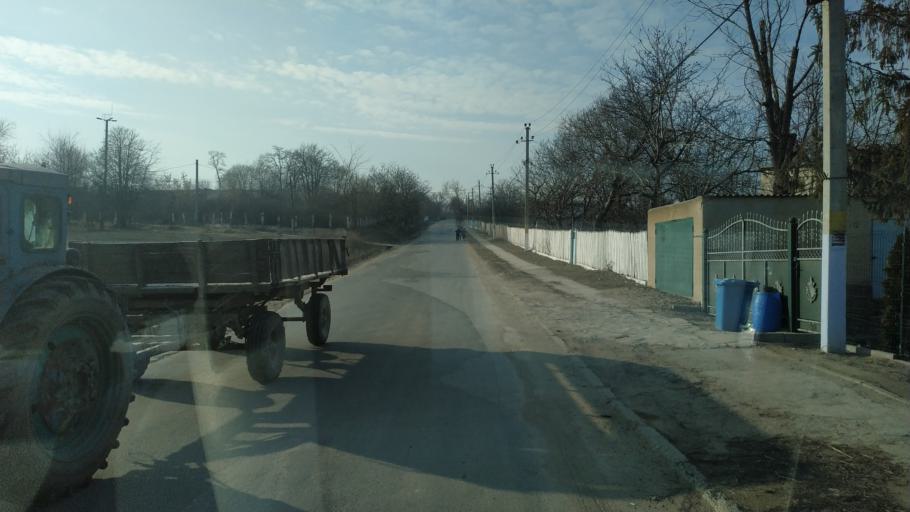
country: MD
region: Hincesti
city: Dancu
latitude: 46.7648
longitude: 28.3453
